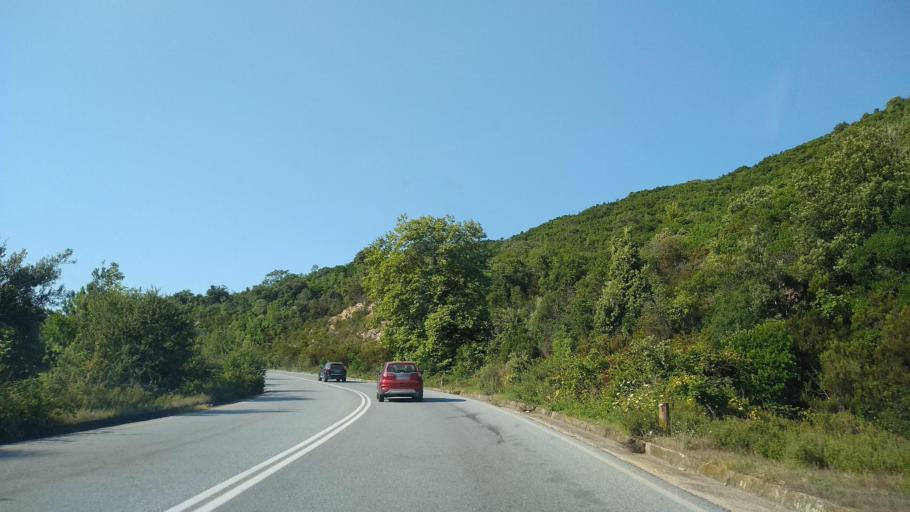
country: GR
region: Central Macedonia
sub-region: Nomos Chalkidikis
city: Stratonion
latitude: 40.5687
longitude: 23.8219
